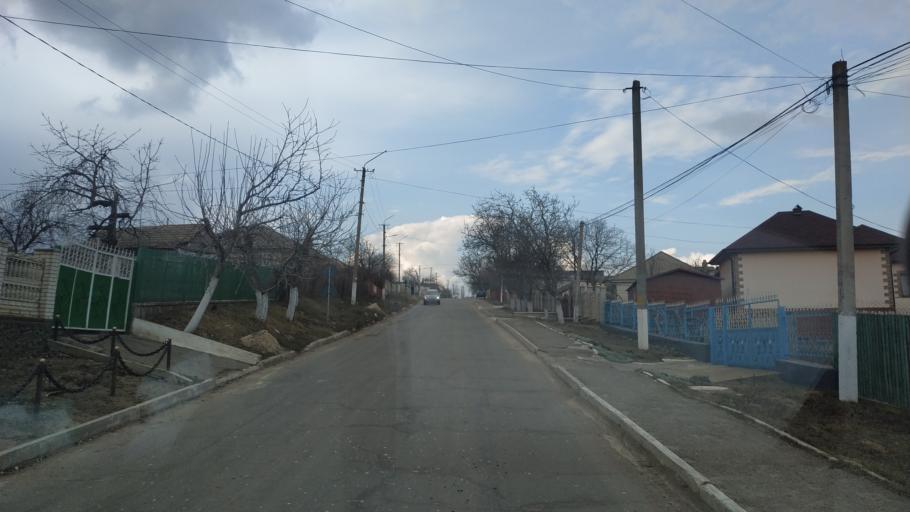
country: MD
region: Anenii Noi
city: Varnita
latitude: 46.8486
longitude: 29.3552
